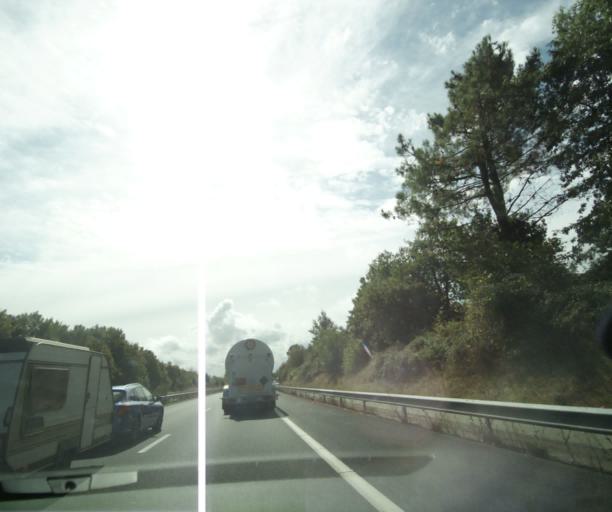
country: FR
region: Poitou-Charentes
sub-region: Departement de la Charente-Maritime
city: Pons
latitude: 45.6038
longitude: -0.5921
